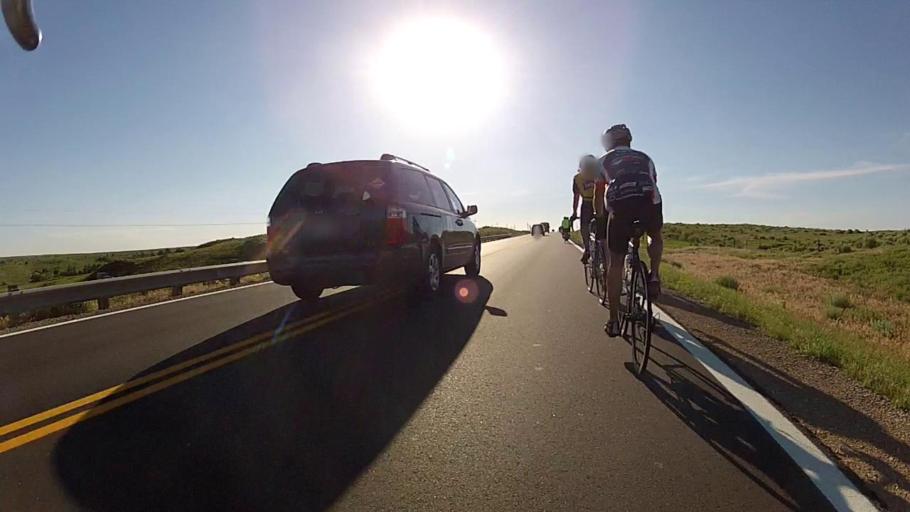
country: US
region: Kansas
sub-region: Comanche County
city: Coldwater
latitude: 37.2806
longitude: -99.0198
